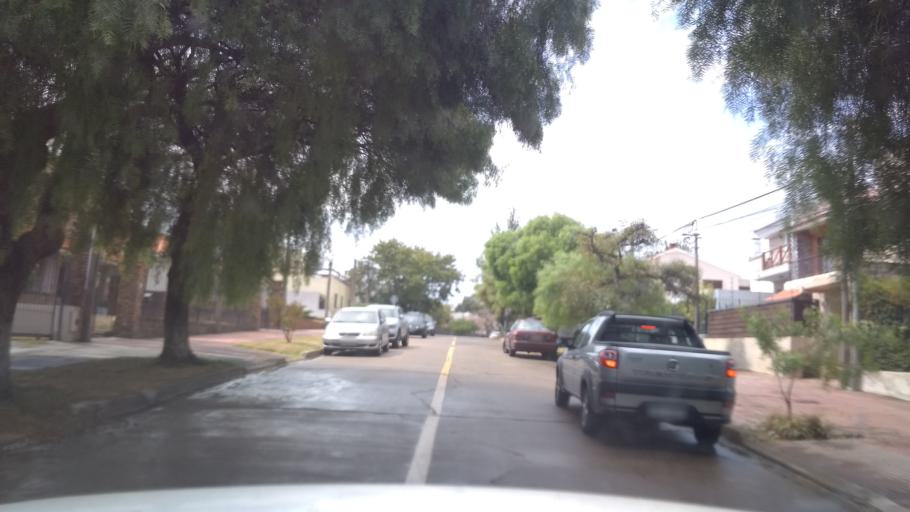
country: UY
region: Canelones
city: Paso de Carrasco
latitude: -34.8968
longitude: -56.0818
